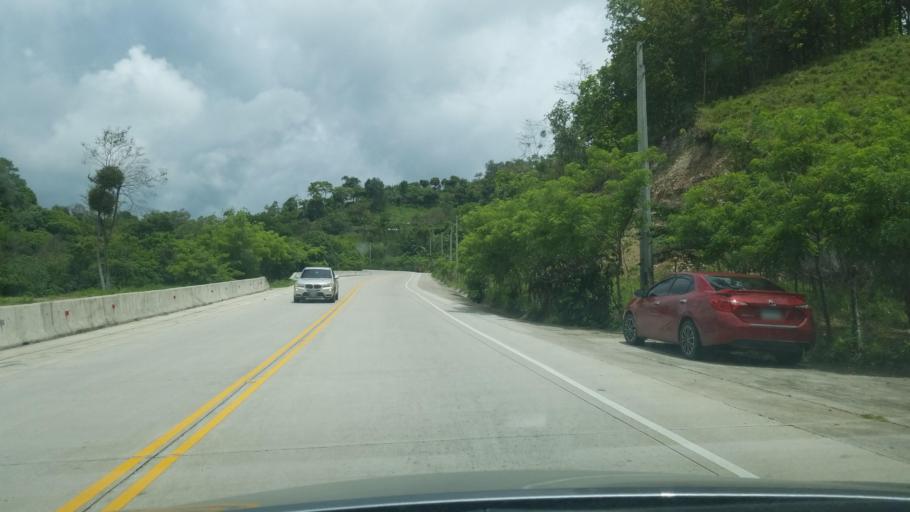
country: HN
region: Copan
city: San Jeronimo
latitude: 14.9925
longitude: -88.8475
